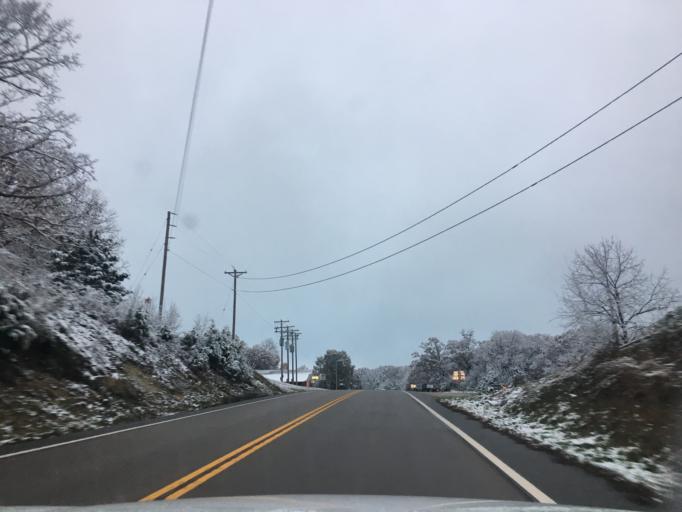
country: US
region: Missouri
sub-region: Osage County
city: Linn
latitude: 38.4737
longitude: -91.7834
